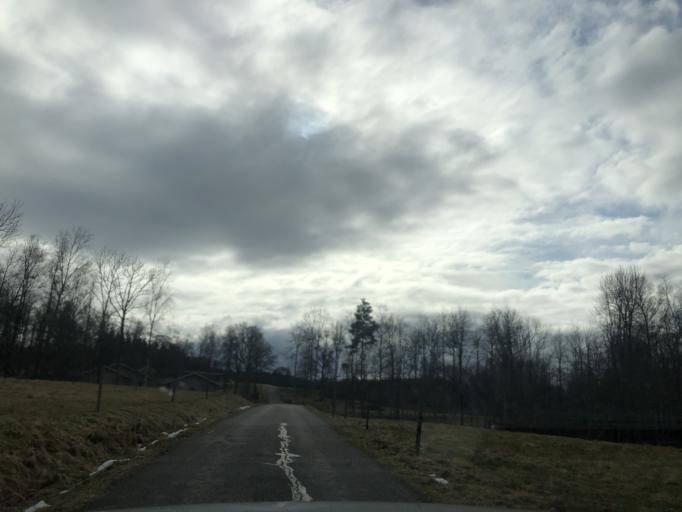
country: SE
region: Vaestra Goetaland
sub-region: Ulricehamns Kommun
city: Ulricehamn
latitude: 57.7676
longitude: 13.4171
